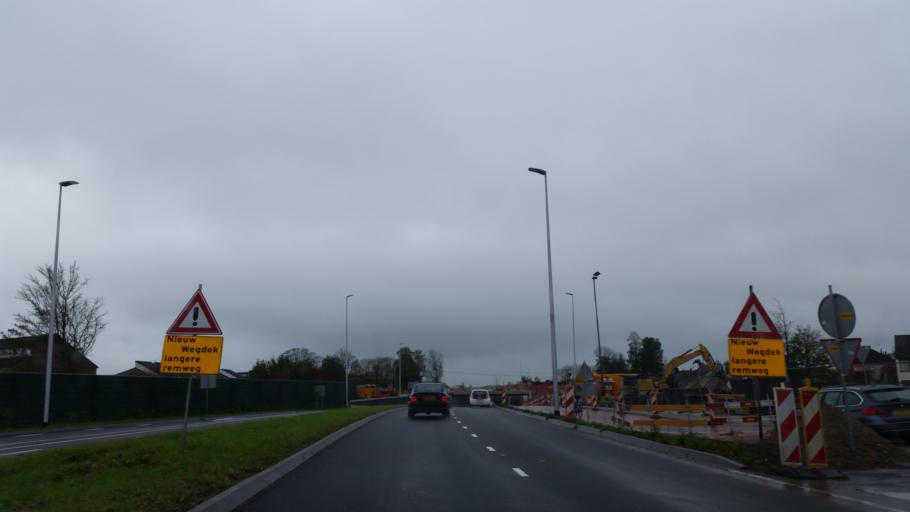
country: NL
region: Friesland
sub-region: Gemeente Leeuwarden
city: Huizum
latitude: 53.1885
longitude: 5.8174
